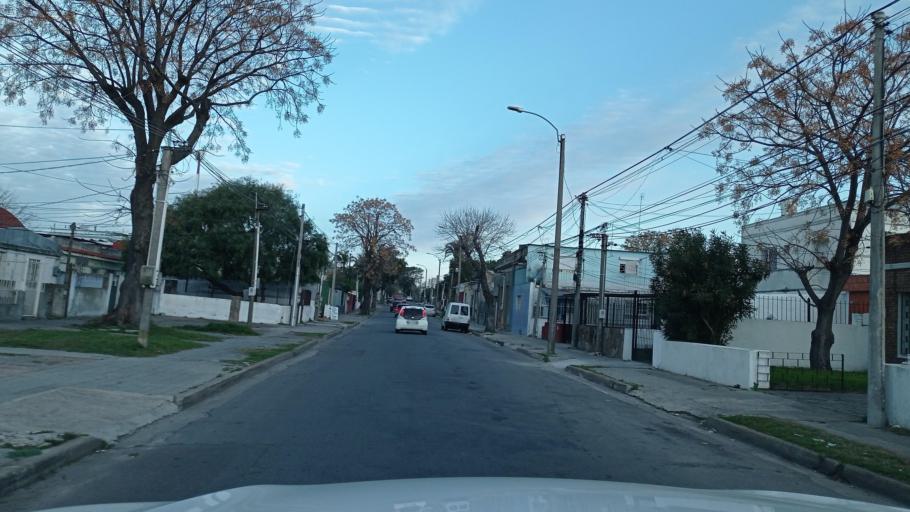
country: UY
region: Montevideo
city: Montevideo
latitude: -34.8691
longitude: -56.1457
